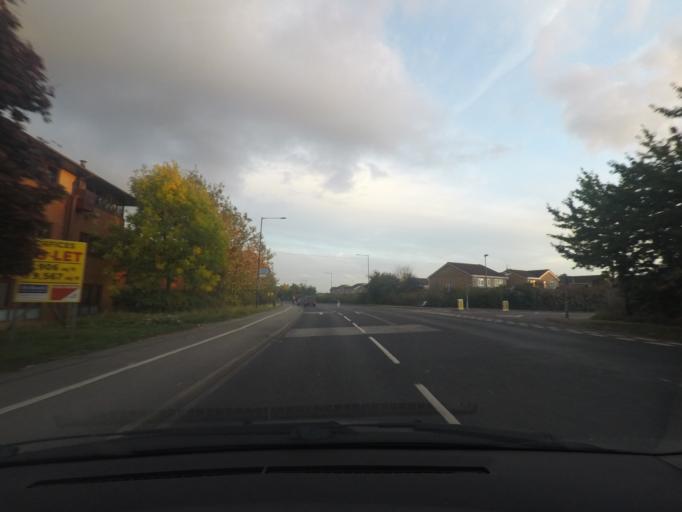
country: GB
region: England
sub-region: City of York
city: Skelton
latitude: 53.9877
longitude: -1.1039
